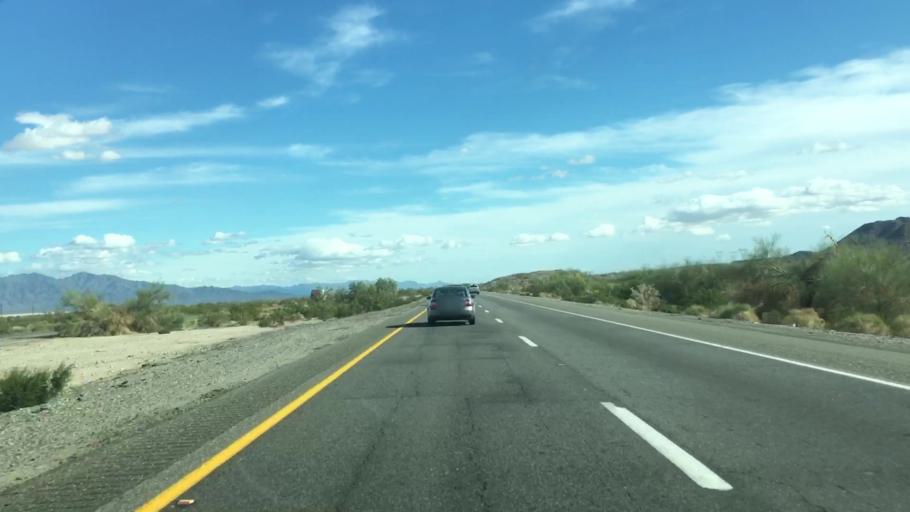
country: US
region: California
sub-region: Imperial County
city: Niland
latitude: 33.7086
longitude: -115.3642
